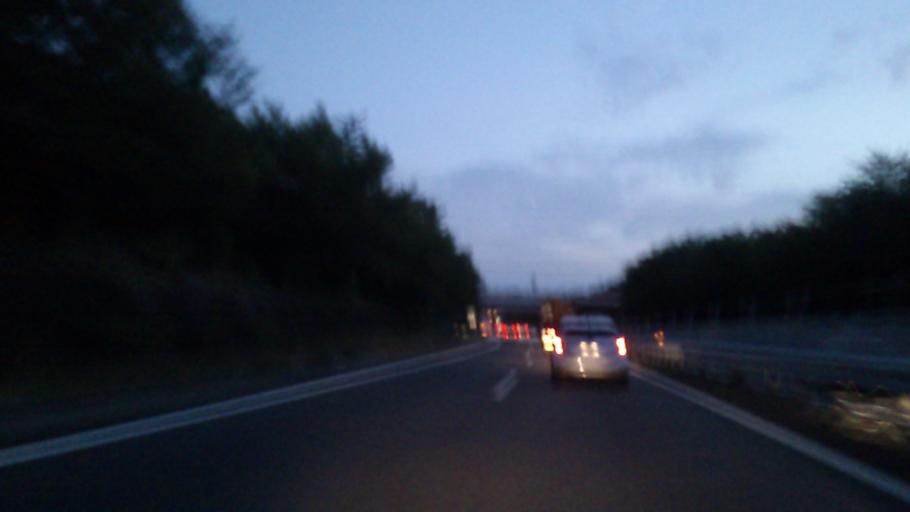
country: JP
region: Aichi
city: Kasugai
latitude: 35.2932
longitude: 136.9850
